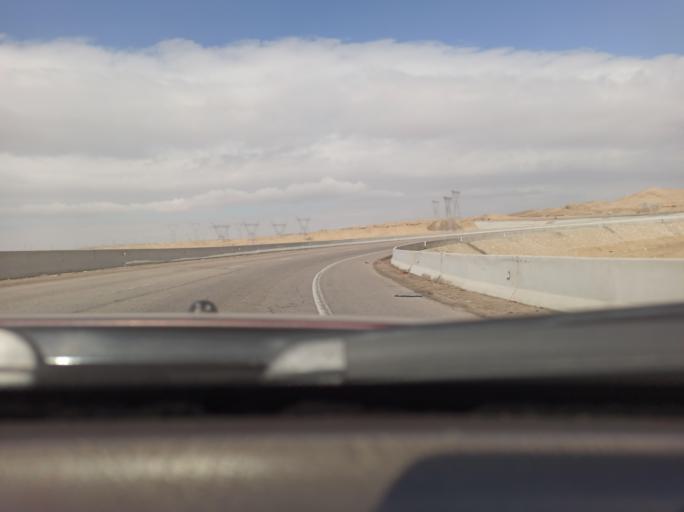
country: EG
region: Muhafazat al Fayyum
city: Tamiyah
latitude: 29.6427
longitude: 31.0120
